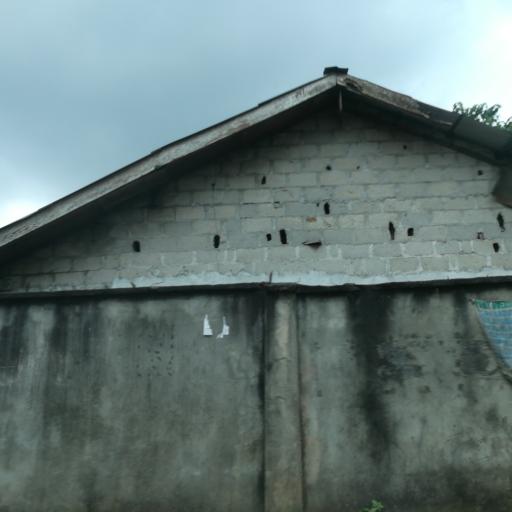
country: NG
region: Rivers
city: Port Harcourt
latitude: 4.8295
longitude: 7.0389
